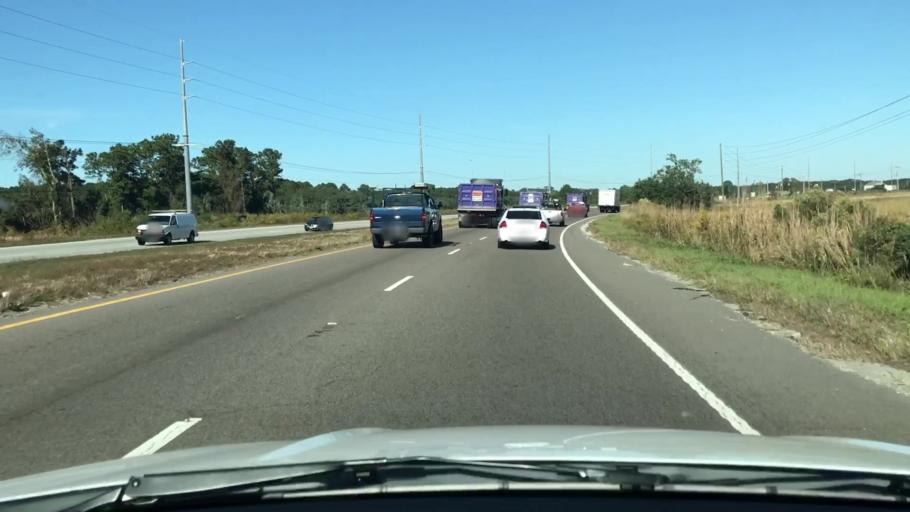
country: US
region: South Carolina
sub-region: Charleston County
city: Shell Point
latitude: 32.7895
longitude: -80.1444
